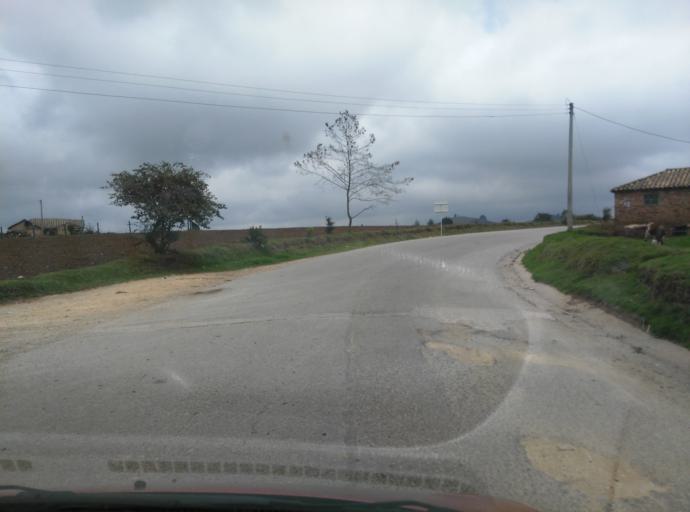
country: CO
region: Boyaca
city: Siachoque
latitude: 5.4914
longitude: -73.2709
